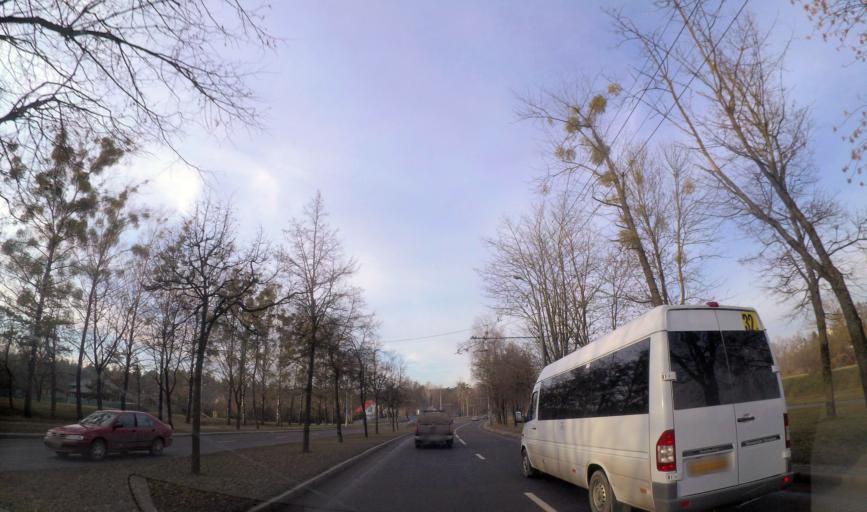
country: BY
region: Grodnenskaya
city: Hrodna
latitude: 53.6841
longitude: 23.8045
